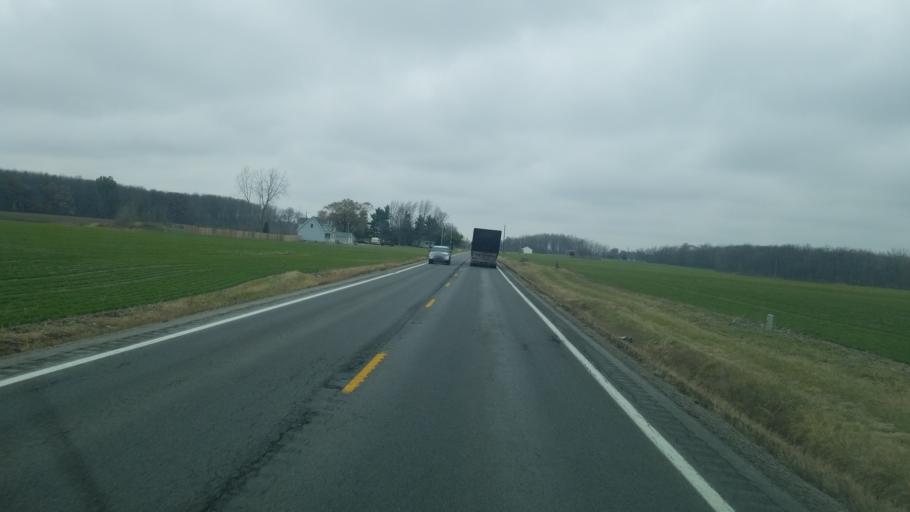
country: US
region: Ohio
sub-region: Huron County
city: Greenwich
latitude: 41.1088
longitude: -82.5008
